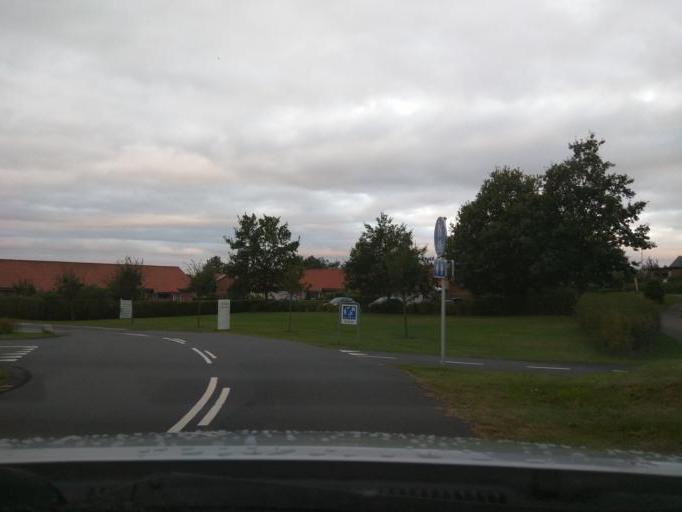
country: DK
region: Central Jutland
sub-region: Viborg Kommune
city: Viborg
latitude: 56.4516
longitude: 9.4481
